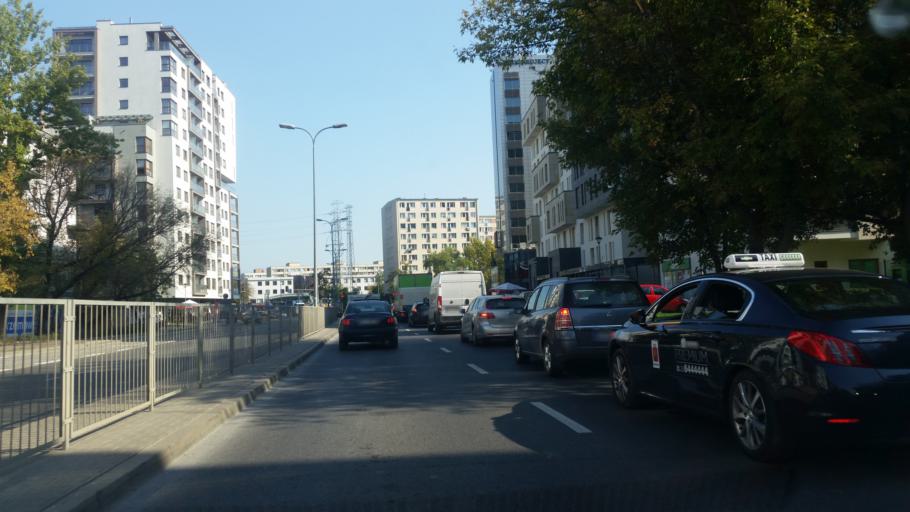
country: PL
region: Masovian Voivodeship
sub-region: Warszawa
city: Mokotow
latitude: 52.1754
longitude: 20.9985
